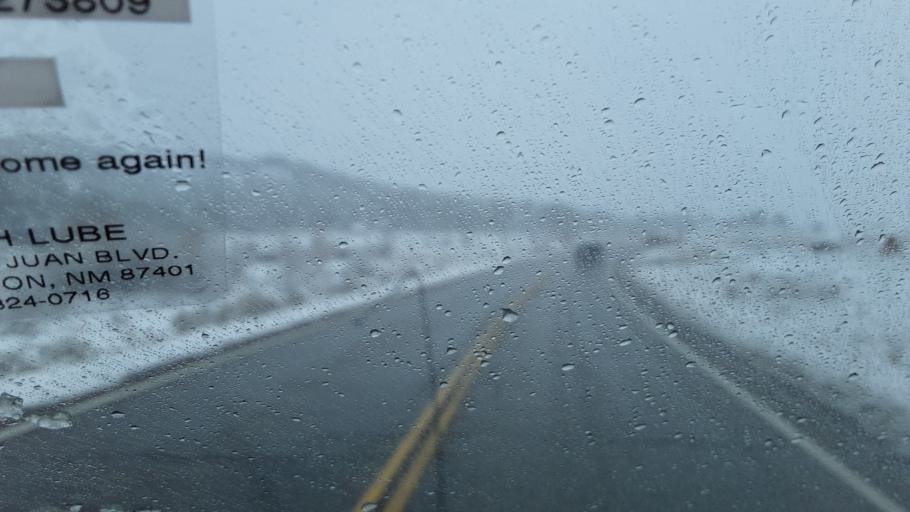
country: US
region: Colorado
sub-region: Archuleta County
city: Pagosa Springs
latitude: 37.2550
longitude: -106.9950
